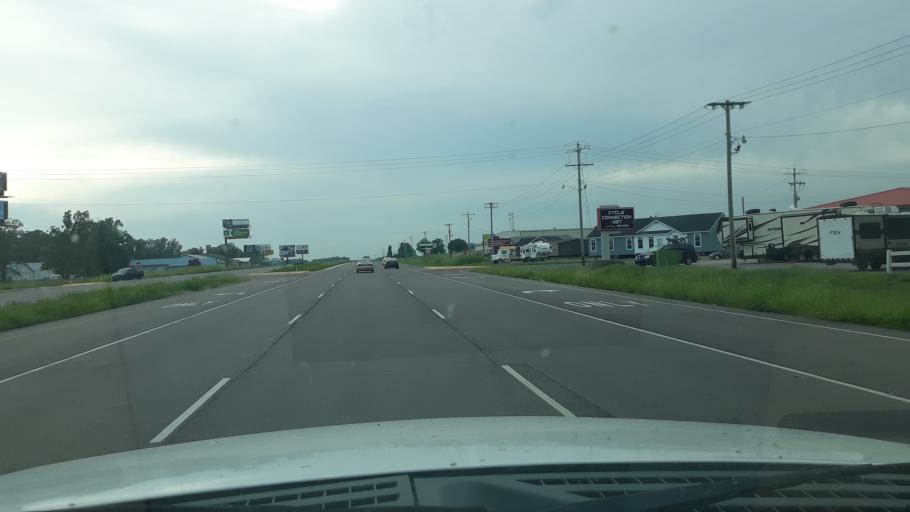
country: US
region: Illinois
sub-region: Williamson County
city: Crainville
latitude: 37.7452
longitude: -89.0434
